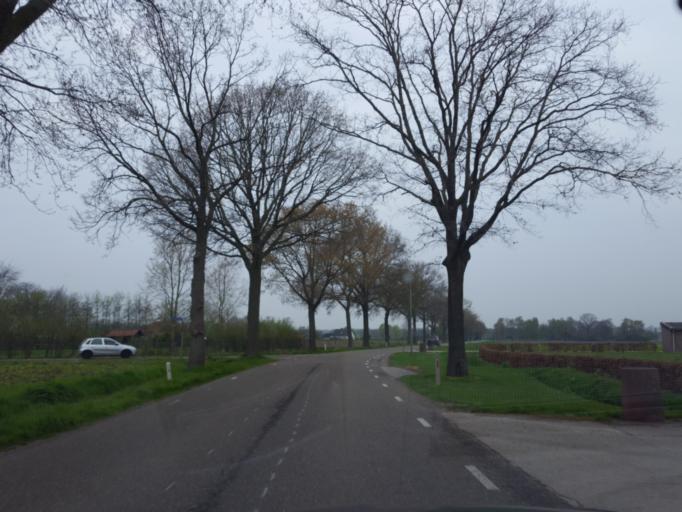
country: NL
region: Limburg
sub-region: Gemeente Nederweert
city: Nederweert
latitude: 51.2970
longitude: 5.7306
